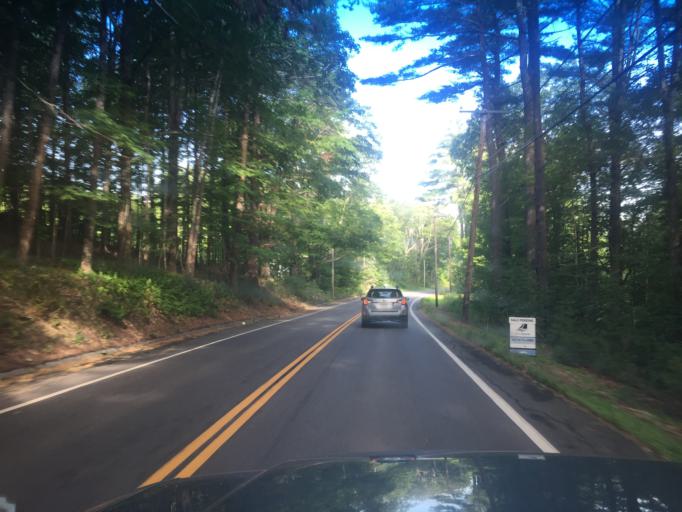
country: US
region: Maine
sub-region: York County
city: South Berwick
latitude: 43.2093
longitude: -70.7834
